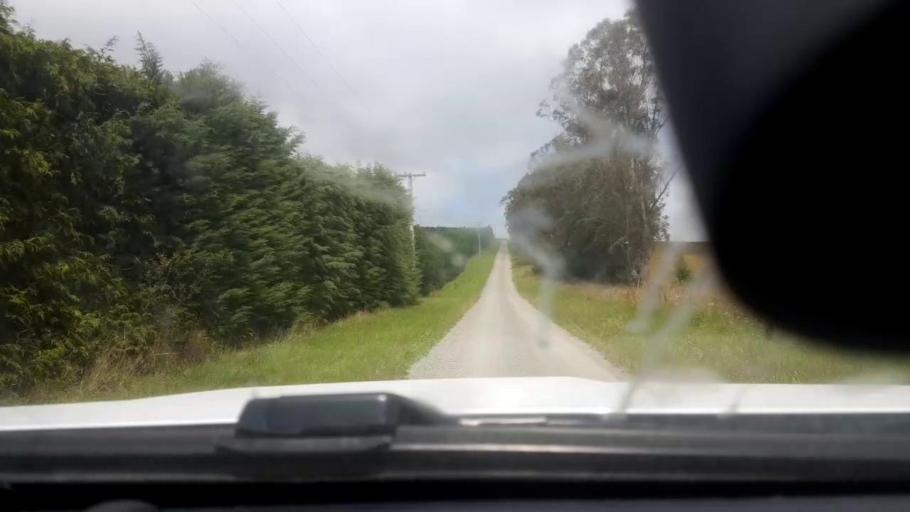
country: NZ
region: Canterbury
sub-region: Timaru District
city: Pleasant Point
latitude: -44.1667
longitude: 171.1466
